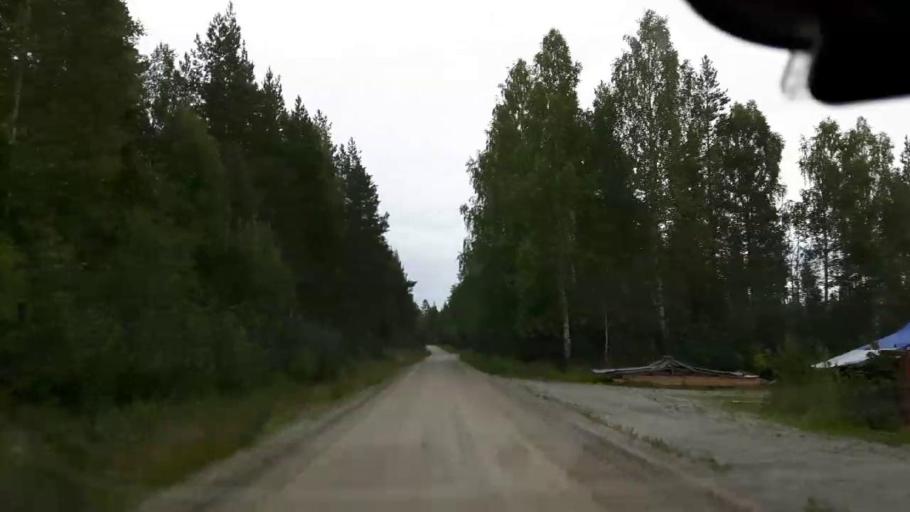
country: SE
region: Jaemtland
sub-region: Braecke Kommun
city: Braecke
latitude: 62.8301
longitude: 15.6914
